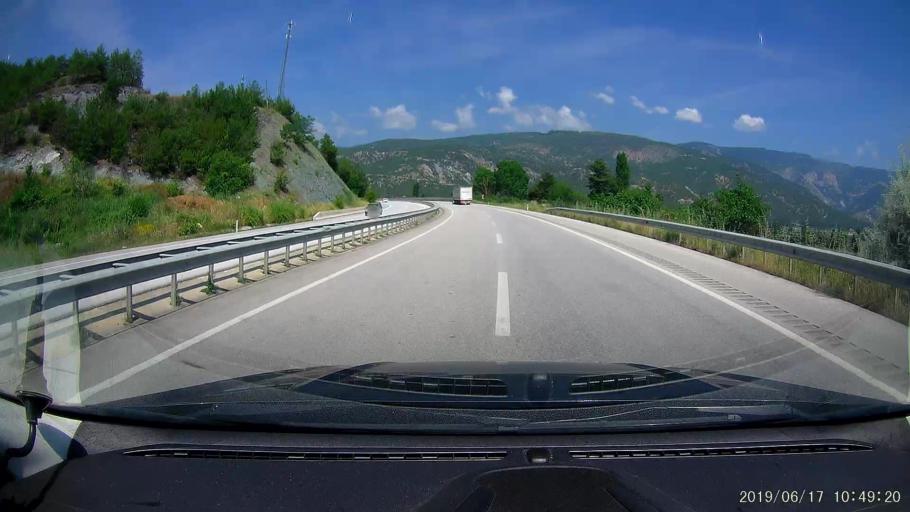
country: TR
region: Corum
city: Hacihamza
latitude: 41.1008
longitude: 34.4125
